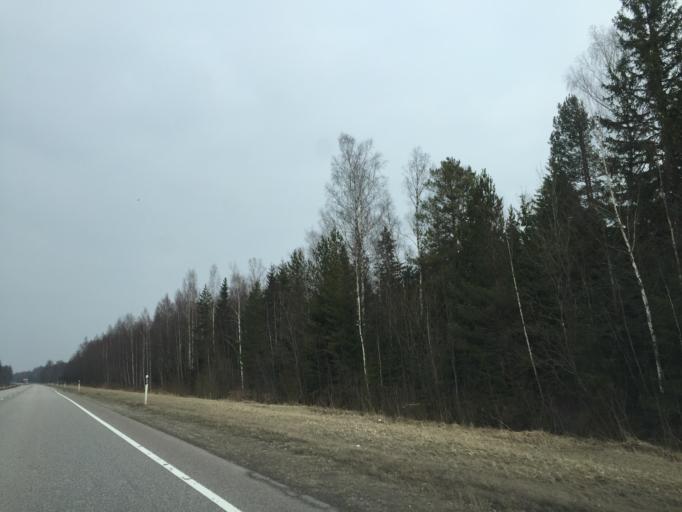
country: LV
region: Salacgrivas
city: Ainazi
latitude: 58.0435
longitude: 24.5090
